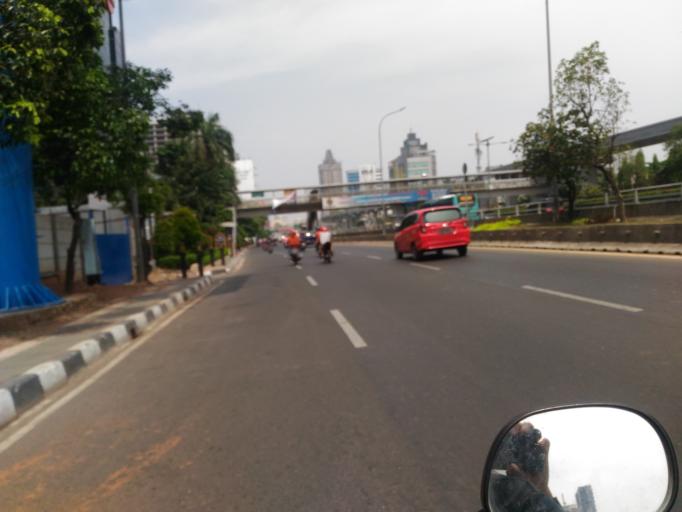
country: ID
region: Jakarta Raya
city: Jakarta
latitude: -6.2430
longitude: 106.8506
